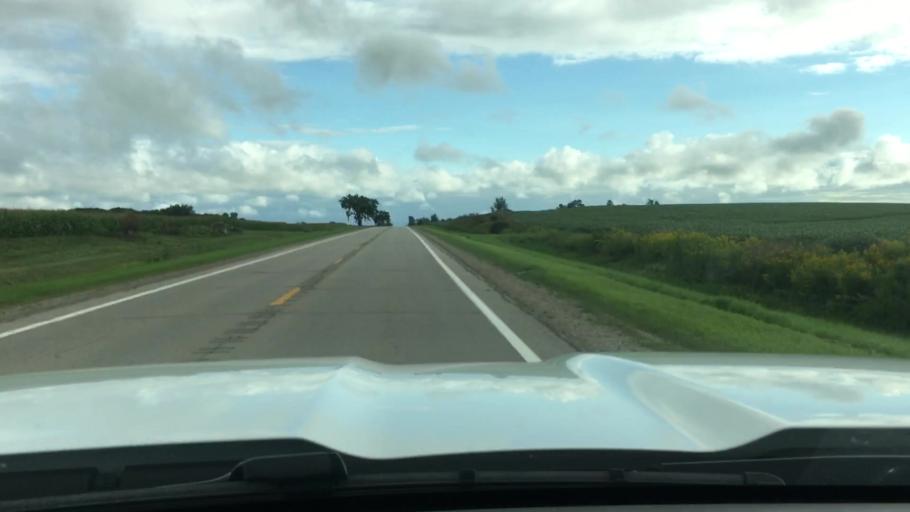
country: US
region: Michigan
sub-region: Tuscola County
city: Caro
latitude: 43.5649
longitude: -83.3076
